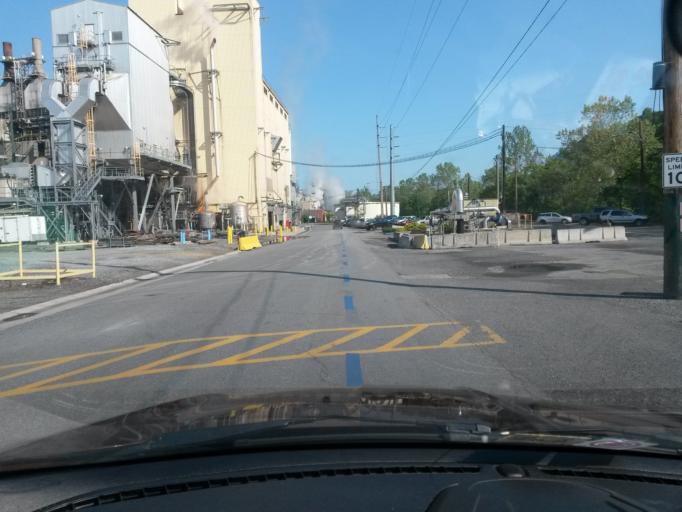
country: US
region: Virginia
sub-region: Rockbridge County
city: Glasgow
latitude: 37.5329
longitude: -79.3549
